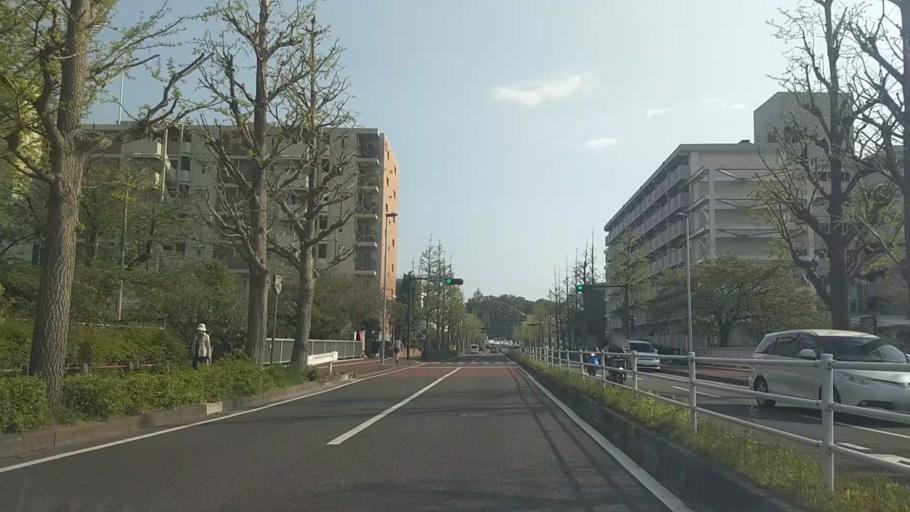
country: JP
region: Kanagawa
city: Kamakura
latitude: 35.3658
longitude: 139.5523
